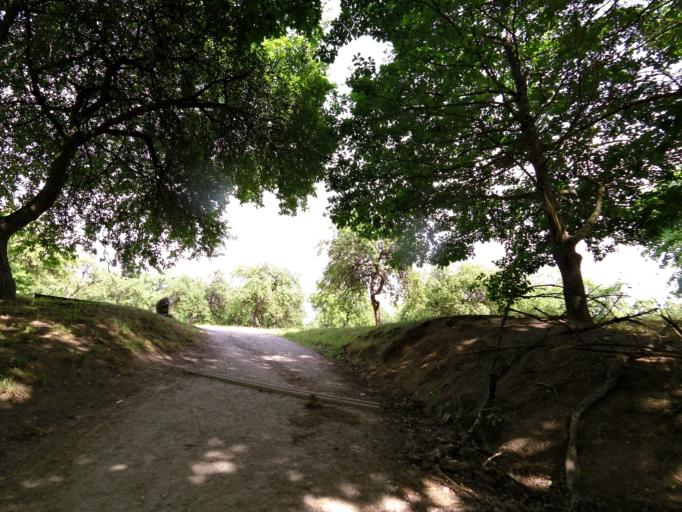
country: LT
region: Vilnius County
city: Rasos
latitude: 54.6883
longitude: 25.3540
